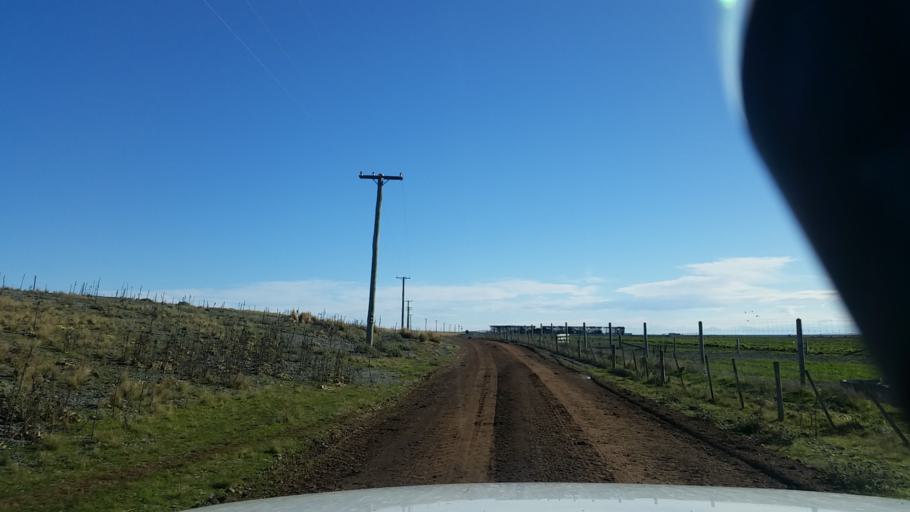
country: NZ
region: Canterbury
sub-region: Selwyn District
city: Lincoln
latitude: -43.8117
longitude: 172.6624
